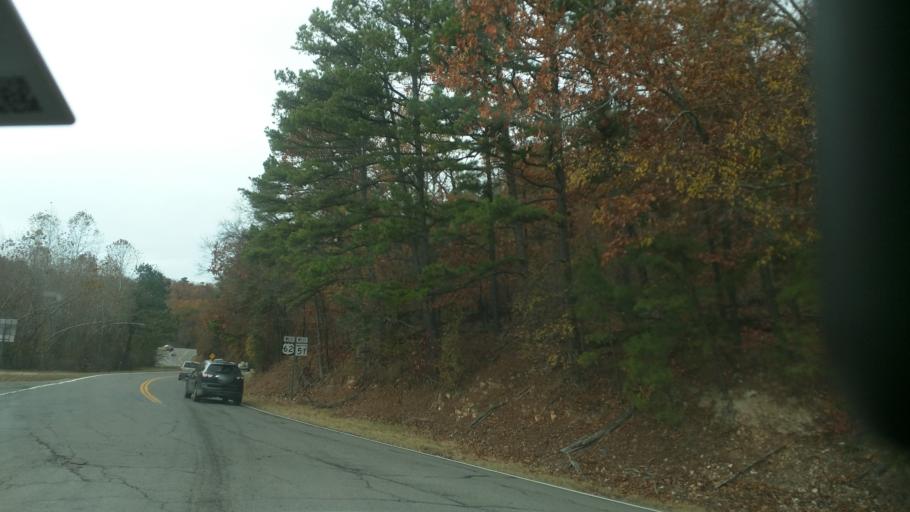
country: US
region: Oklahoma
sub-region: Cherokee County
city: Tahlequah
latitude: 35.9280
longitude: -94.8403
